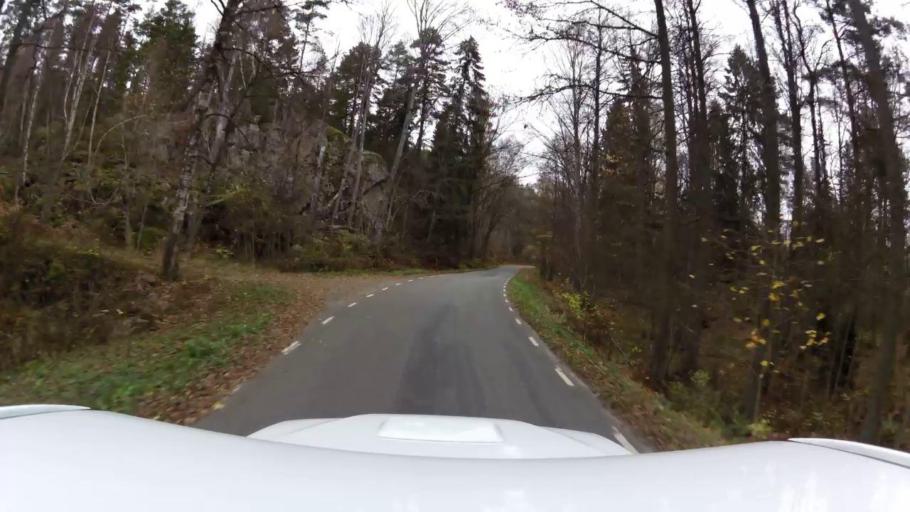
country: SE
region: OEstergoetland
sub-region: Kinda Kommun
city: Rimforsa
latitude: 58.1400
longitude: 15.6333
